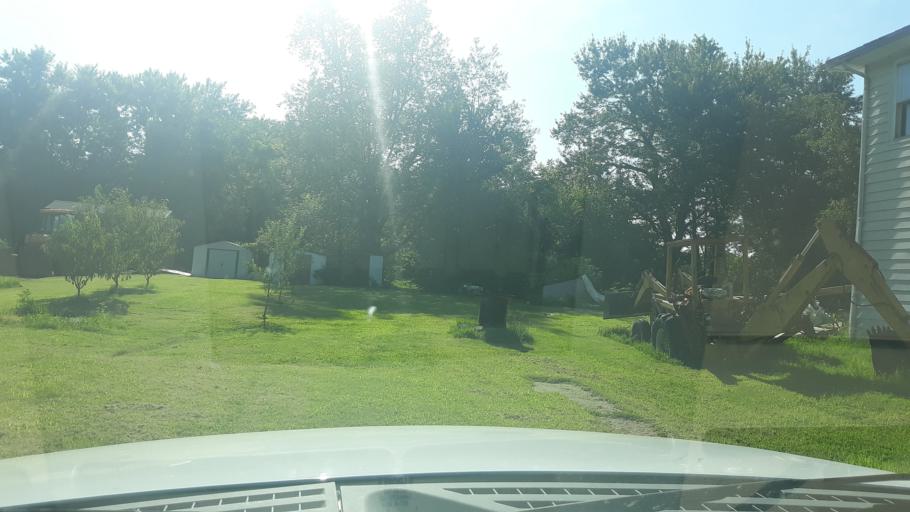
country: US
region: Illinois
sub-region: Saline County
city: Harrisburg
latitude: 37.8378
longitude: -88.6134
